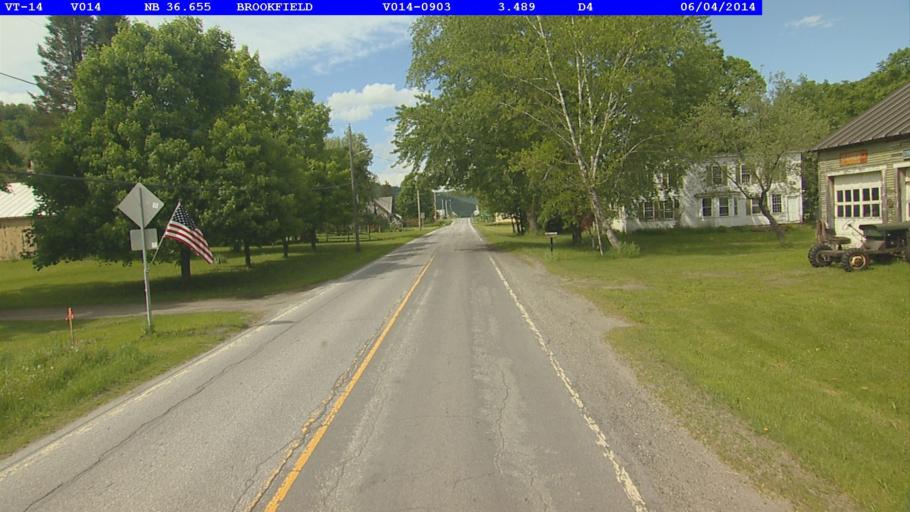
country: US
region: Vermont
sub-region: Orange County
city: Williamstown
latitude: 44.0273
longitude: -72.5709
